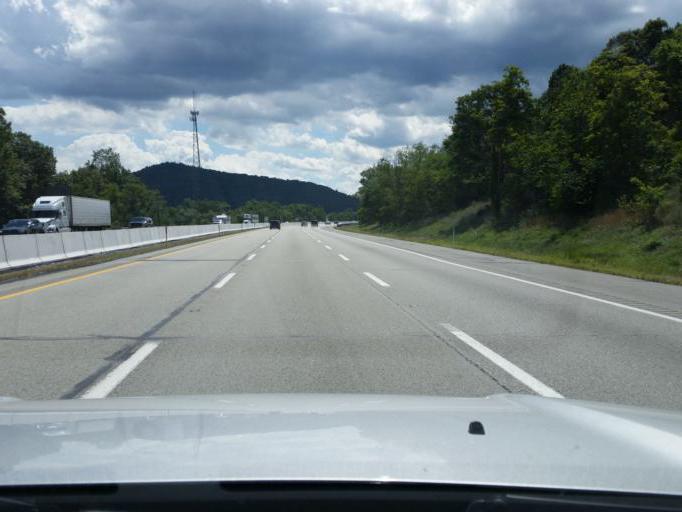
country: US
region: Pennsylvania
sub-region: Fulton County
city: McConnellsburg
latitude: 40.0563
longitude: -78.0986
